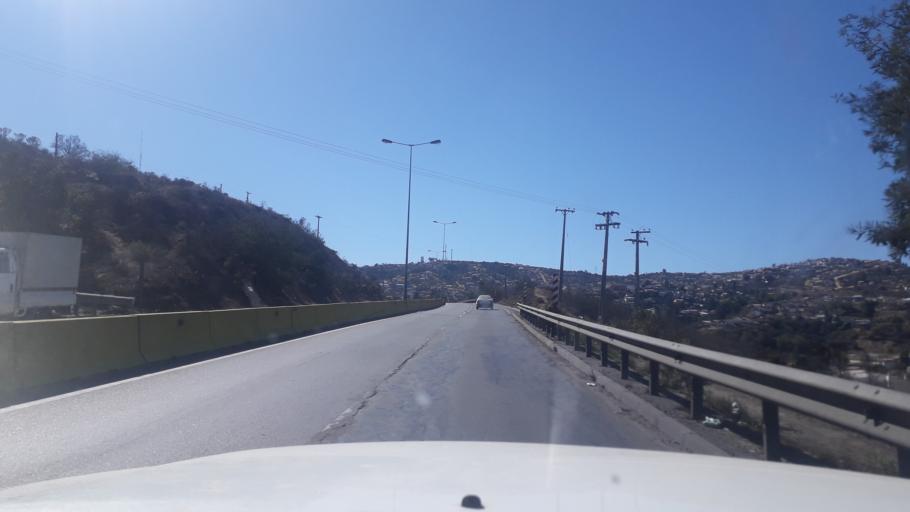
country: CL
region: Valparaiso
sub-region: Provincia de Valparaiso
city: Vina del Mar
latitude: -33.0307
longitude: -71.5002
